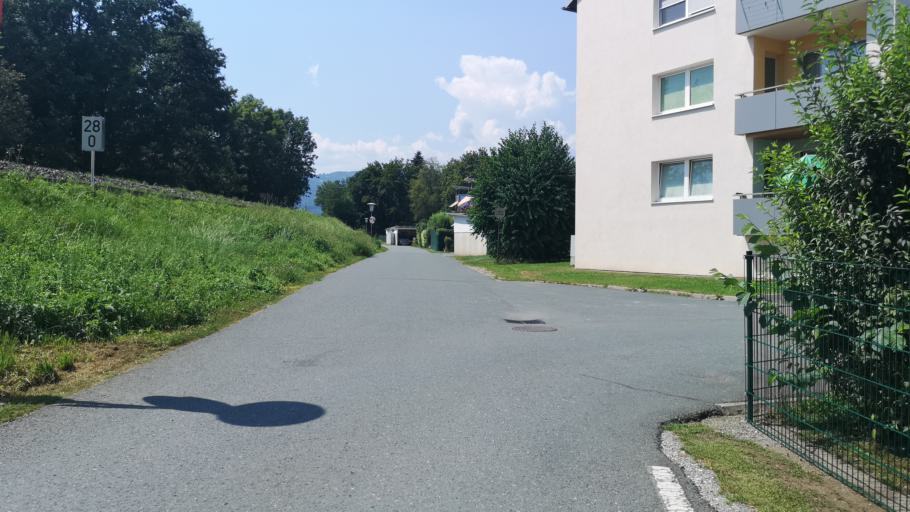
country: AT
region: Styria
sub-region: Politischer Bezirk Deutschlandsberg
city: Deutschlandsberg
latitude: 46.8241
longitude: 15.2487
